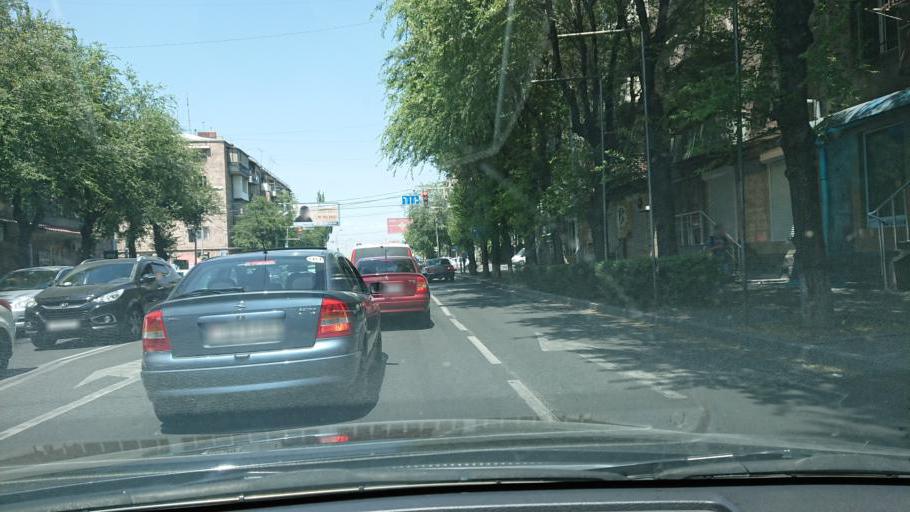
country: AM
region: Yerevan
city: Yerevan
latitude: 40.2045
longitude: 44.4976
